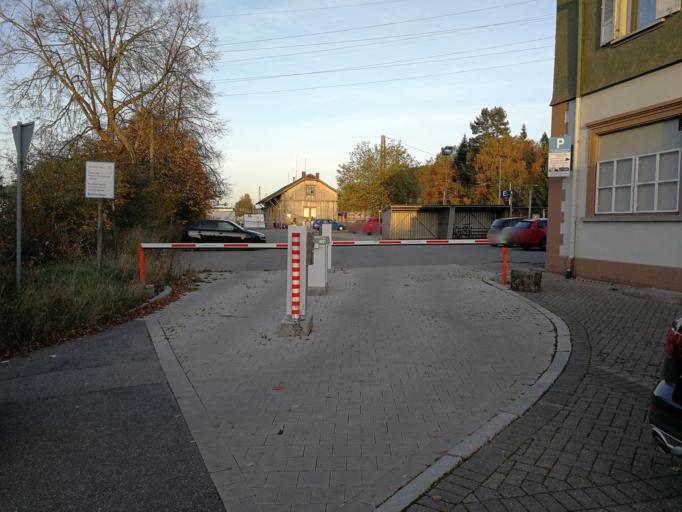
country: DE
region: Baden-Wuerttemberg
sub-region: Freiburg Region
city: Sankt Georgen im Schwarzwald
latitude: 48.1242
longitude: 8.3420
